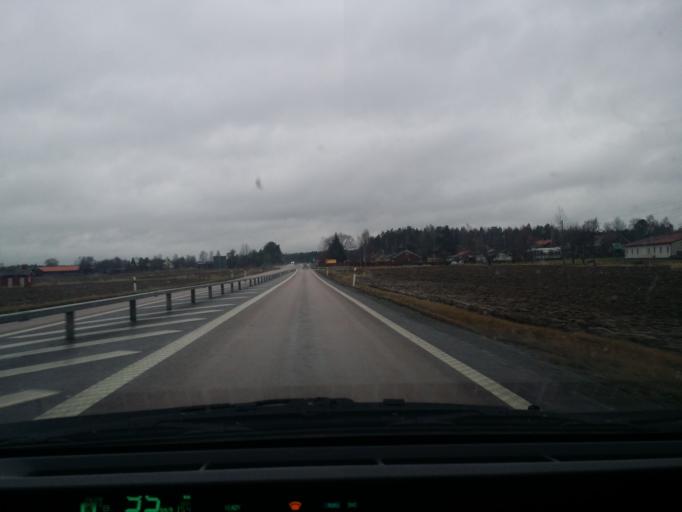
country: SE
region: Vaestmanland
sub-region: Sala Kommun
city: Sala
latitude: 59.8704
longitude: 16.5423
